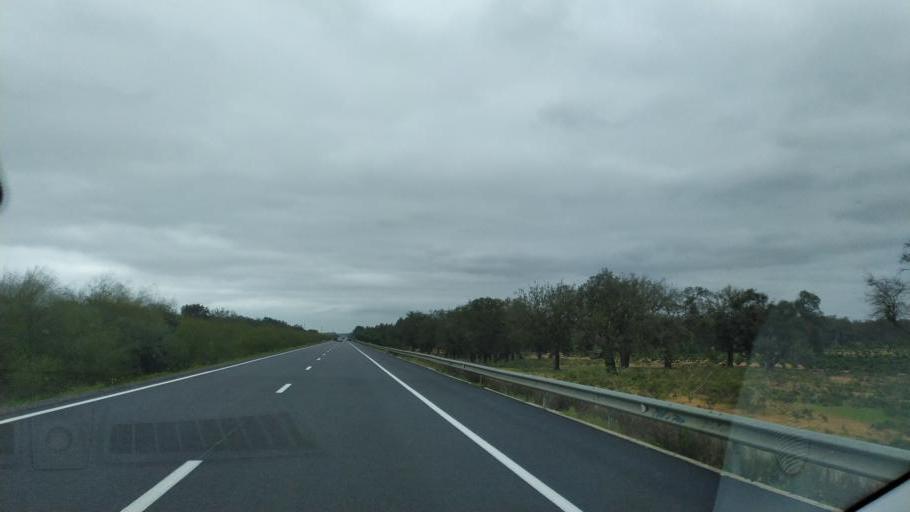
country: MA
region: Gharb-Chrarda-Beni Hssen
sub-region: Kenitra Province
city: Kenitra
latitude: 34.1767
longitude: -6.6560
